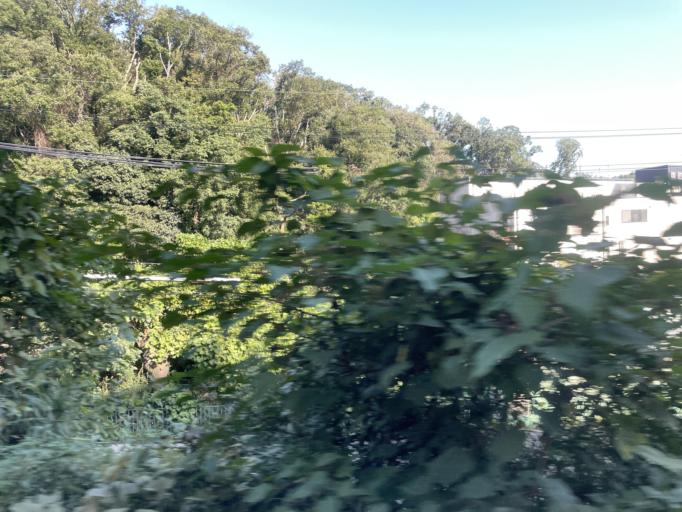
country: JP
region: Osaka
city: Kashihara
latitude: 34.5414
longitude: 135.6687
